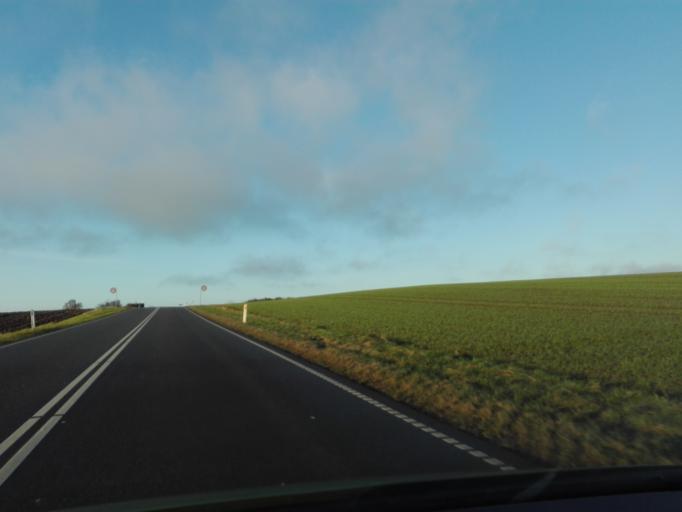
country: DK
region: Central Jutland
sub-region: Skanderborg Kommune
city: Skanderborg
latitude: 56.0627
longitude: 9.9010
